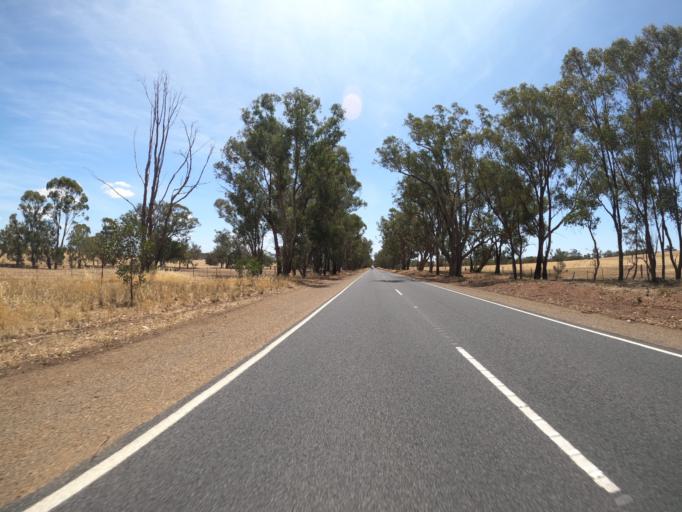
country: AU
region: Victoria
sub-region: Benalla
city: Benalla
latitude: -36.3650
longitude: 145.9696
